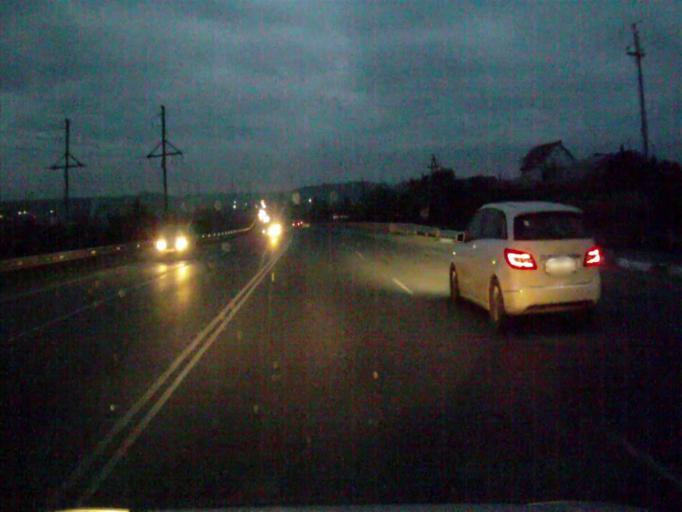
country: RU
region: Chelyabinsk
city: Sargazy
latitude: 55.1420
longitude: 61.2643
